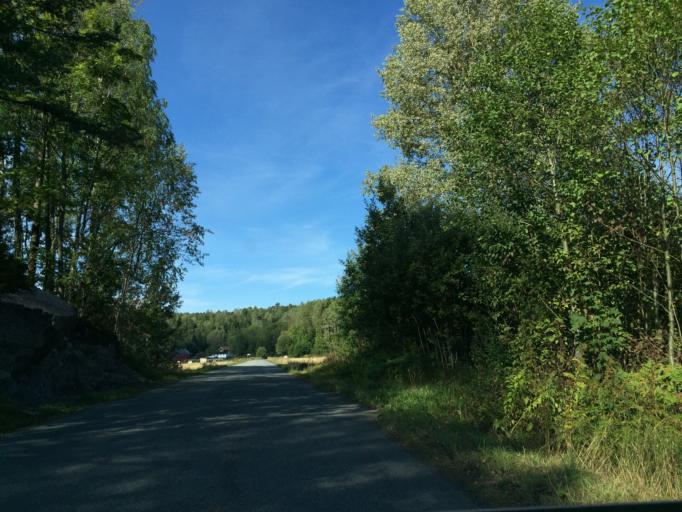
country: NO
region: Vestfold
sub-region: Holmestrand
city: Gullhaug
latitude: 59.4840
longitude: 10.1661
